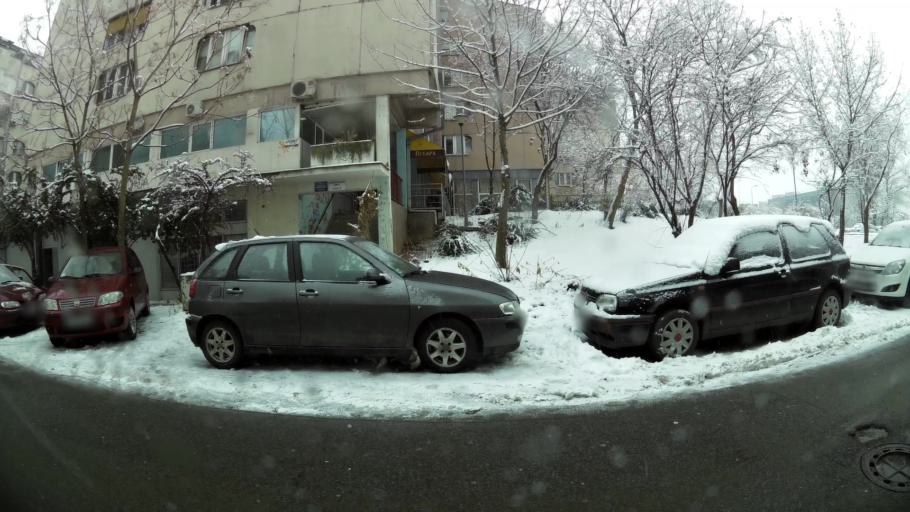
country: RS
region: Central Serbia
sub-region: Belgrade
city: Novi Beograd
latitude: 44.8130
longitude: 20.4112
